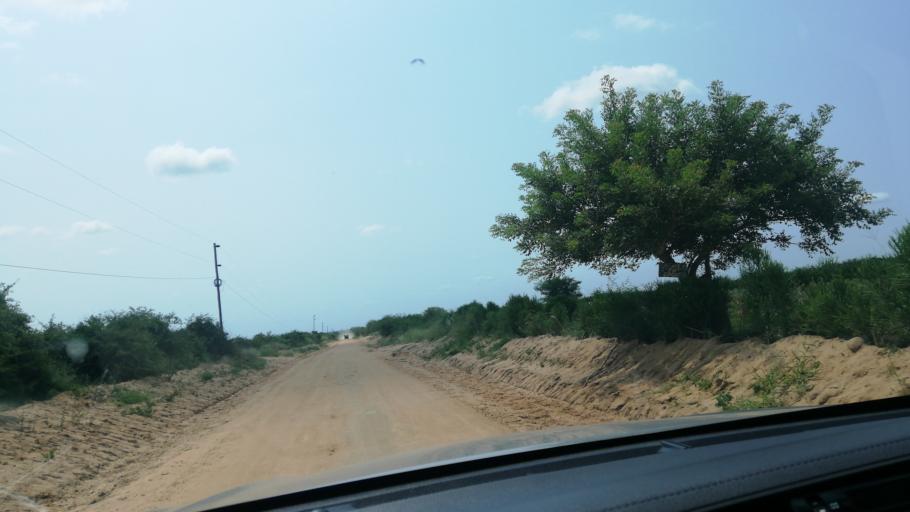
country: MZ
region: Maputo
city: Matola
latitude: -26.0952
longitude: 32.3896
